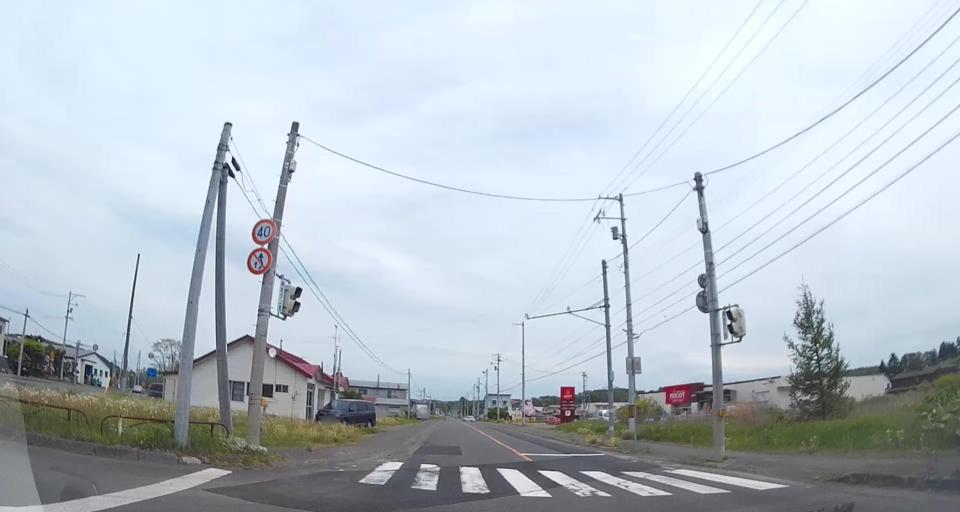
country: JP
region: Hokkaido
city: Chitose
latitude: 42.7680
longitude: 141.8209
